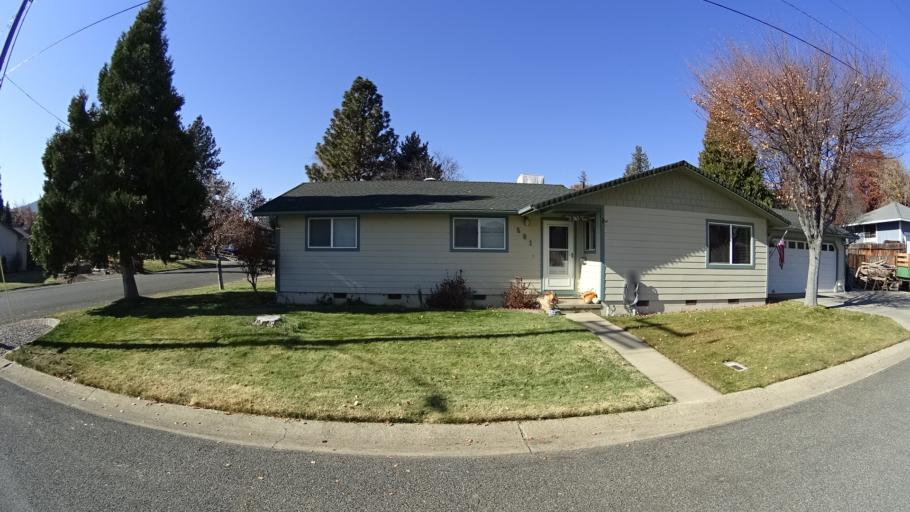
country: US
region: California
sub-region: Siskiyou County
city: Yreka
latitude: 41.7370
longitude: -122.6421
